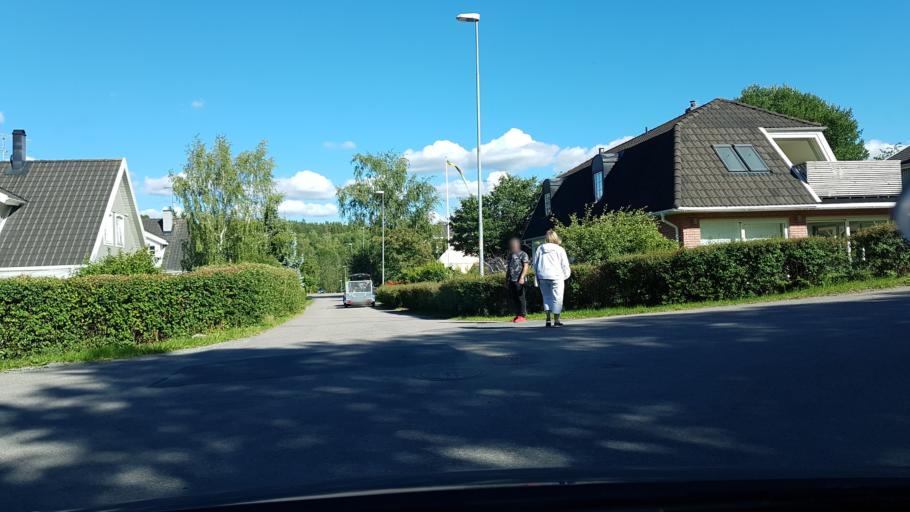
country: SE
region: Stockholm
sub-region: Upplands-Bro Kommun
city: Kungsaengen
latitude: 59.4781
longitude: 17.8007
